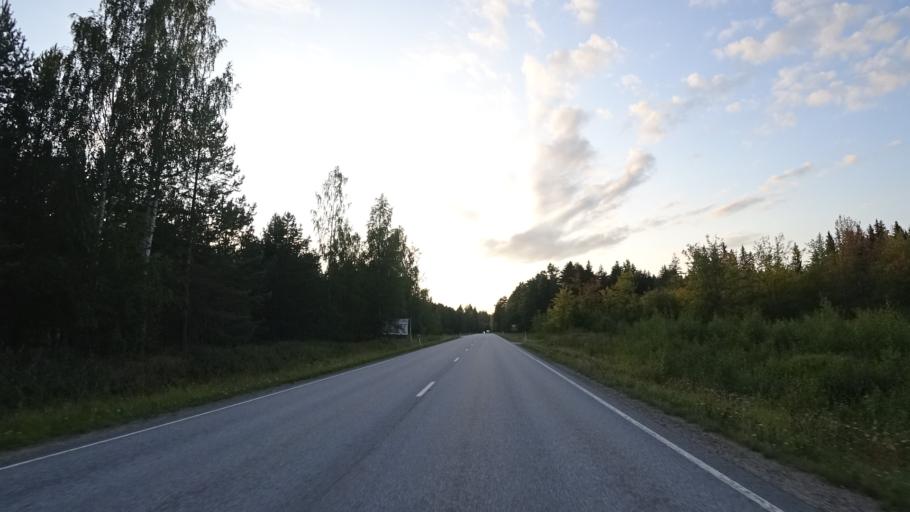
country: FI
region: Southern Savonia
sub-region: Savonlinna
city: Punkaharju
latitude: 61.7995
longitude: 29.3256
